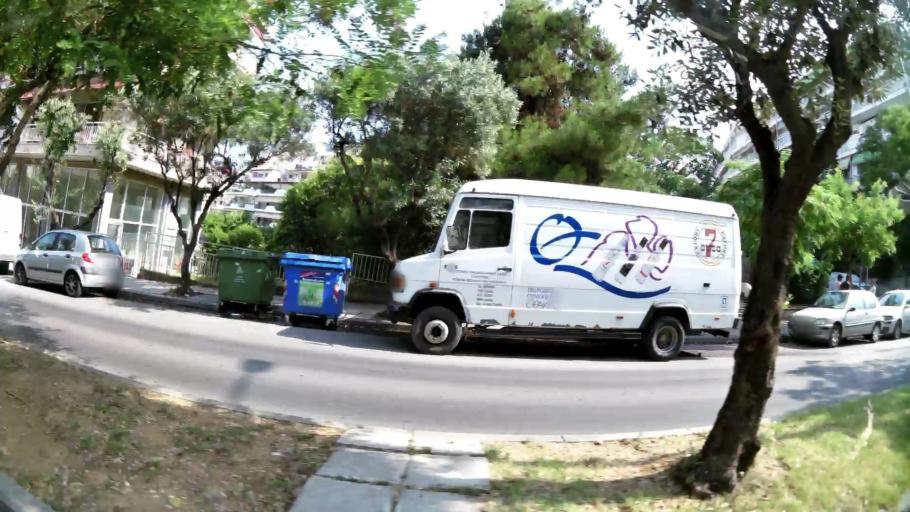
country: GR
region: Central Macedonia
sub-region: Nomos Thessalonikis
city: Sykies
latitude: 40.6507
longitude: 22.9565
